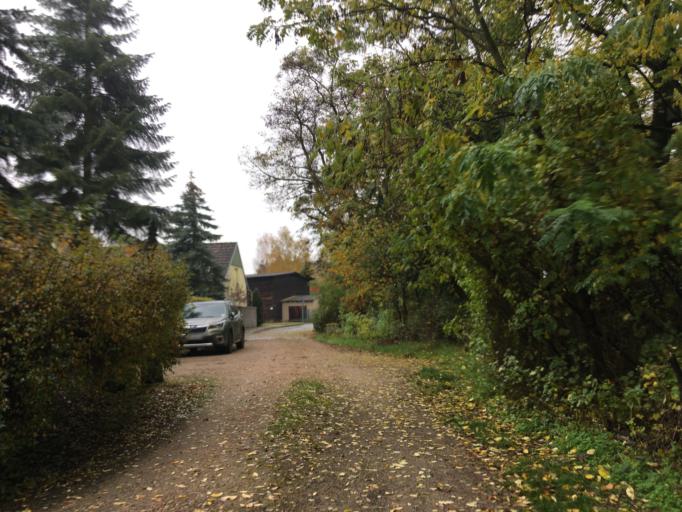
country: DE
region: Brandenburg
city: Briesen
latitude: 52.2657
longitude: 14.2927
